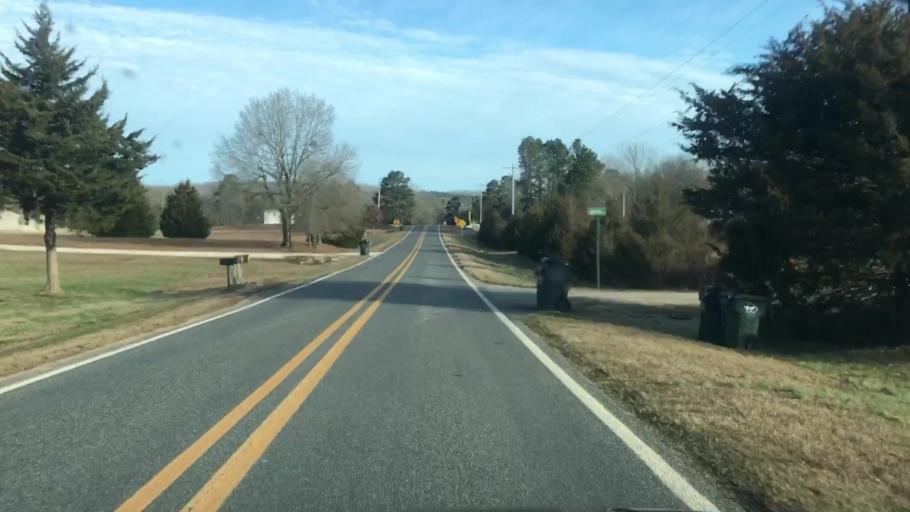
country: US
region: Arkansas
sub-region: Garland County
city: Rockwell
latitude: 34.5055
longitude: -93.2762
